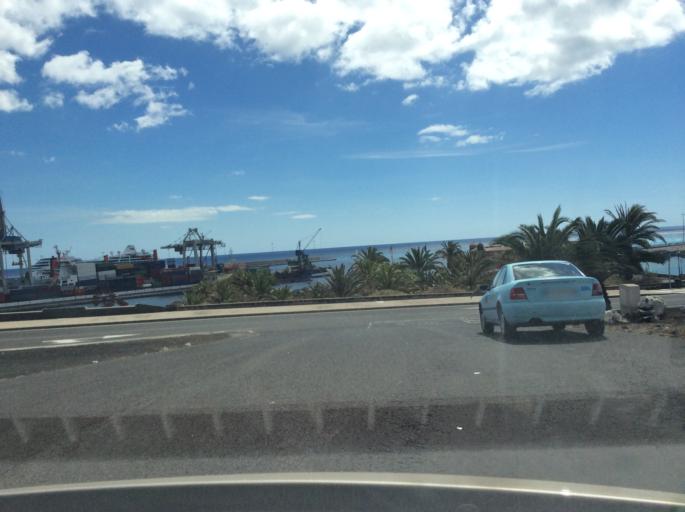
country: ES
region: Canary Islands
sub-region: Provincia de Las Palmas
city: Arrecife
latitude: 28.9723
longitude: -13.5335
